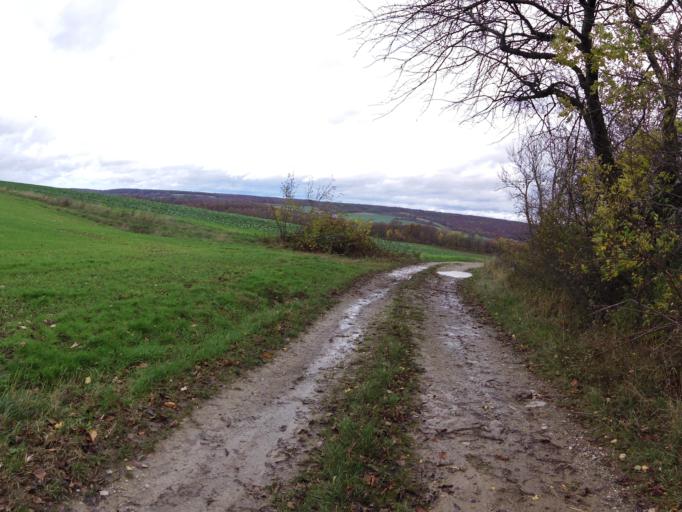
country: DE
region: Thuringia
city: Ifta
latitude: 51.0650
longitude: 10.1348
